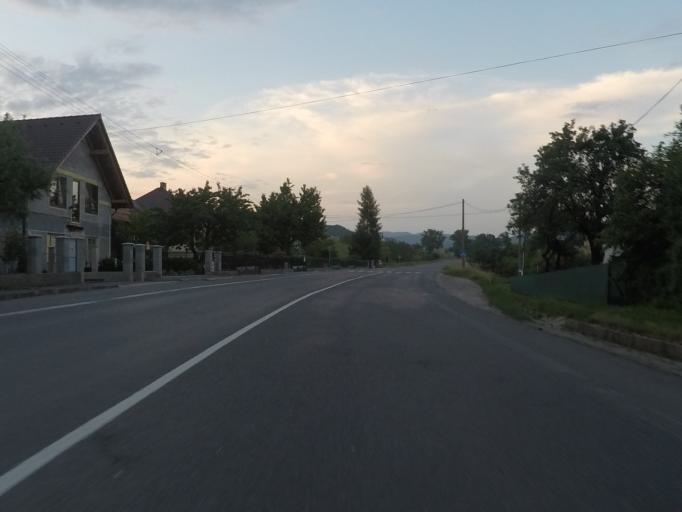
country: SK
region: Banskobystricky
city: Rimavska Sobota
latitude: 48.5011
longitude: 19.9355
